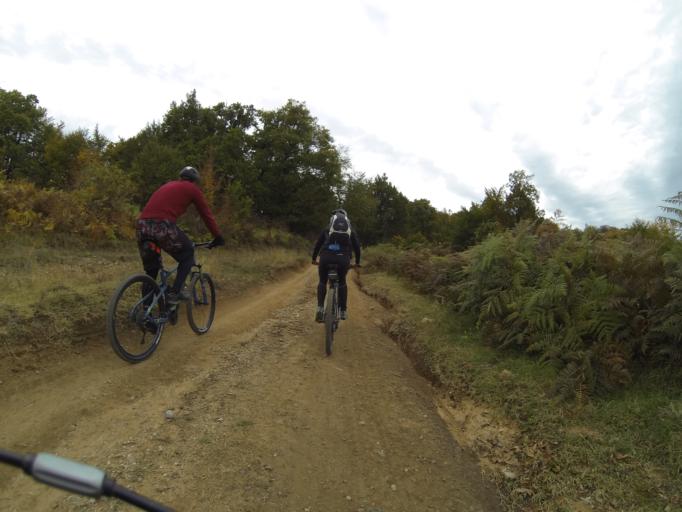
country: RO
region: Gorj
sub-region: Comuna Tismana
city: Sohodol
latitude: 45.0695
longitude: 22.8621
